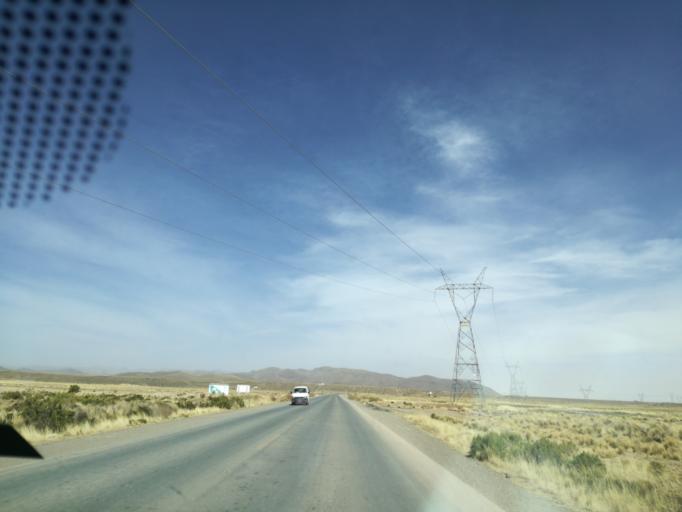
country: BO
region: Oruro
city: Oruro
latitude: -17.8079
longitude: -67.0216
